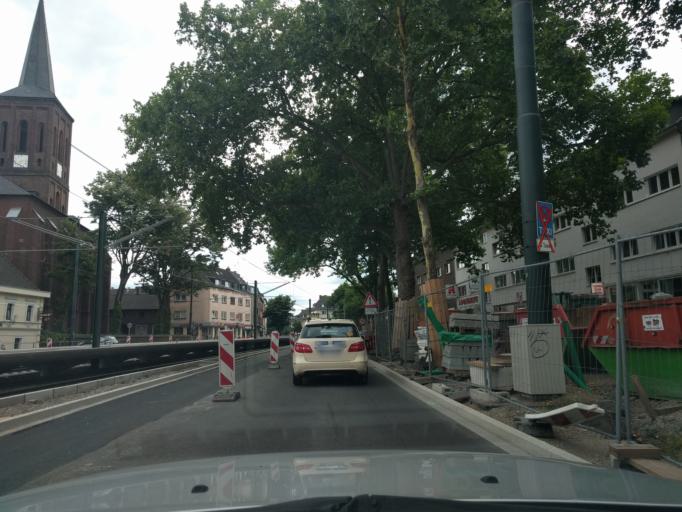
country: DE
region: North Rhine-Westphalia
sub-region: Regierungsbezirk Dusseldorf
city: Neuss
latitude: 51.2322
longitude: 6.7226
